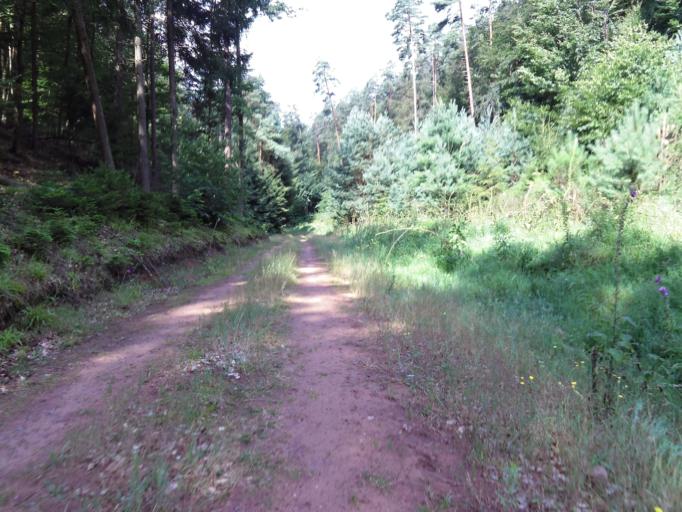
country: DE
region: Rheinland-Pfalz
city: Neidenfels
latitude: 49.4252
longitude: 8.0734
